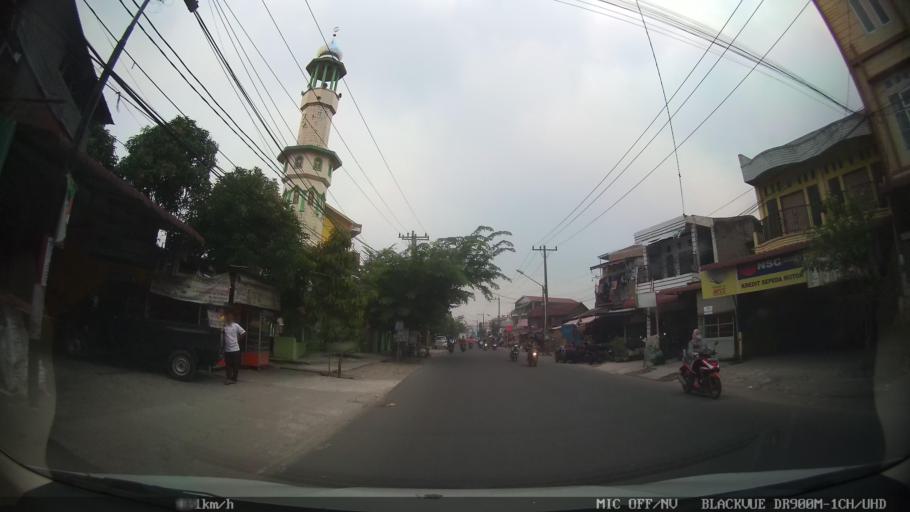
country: ID
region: North Sumatra
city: Medan
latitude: 3.5776
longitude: 98.7277
